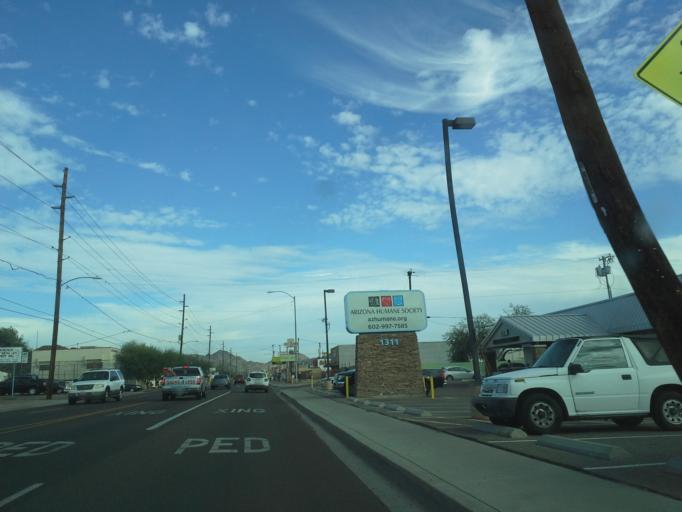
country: US
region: Arizona
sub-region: Maricopa County
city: Glendale
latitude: 33.5712
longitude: -112.0901
